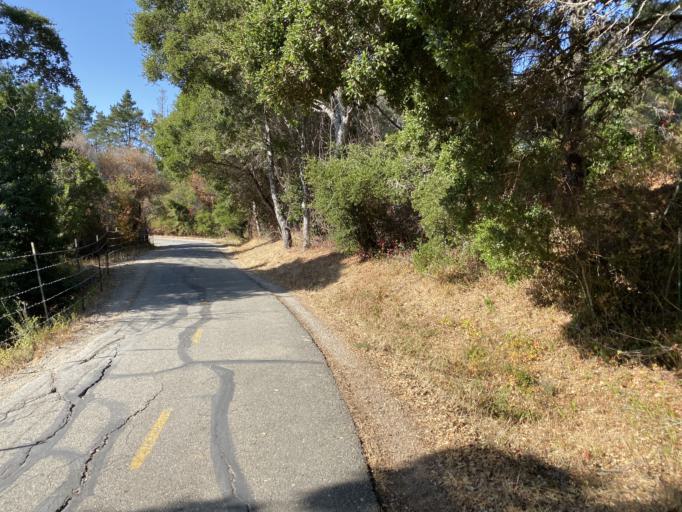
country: US
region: California
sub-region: San Mateo County
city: Hillsborough
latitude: 37.5589
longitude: -122.3922
